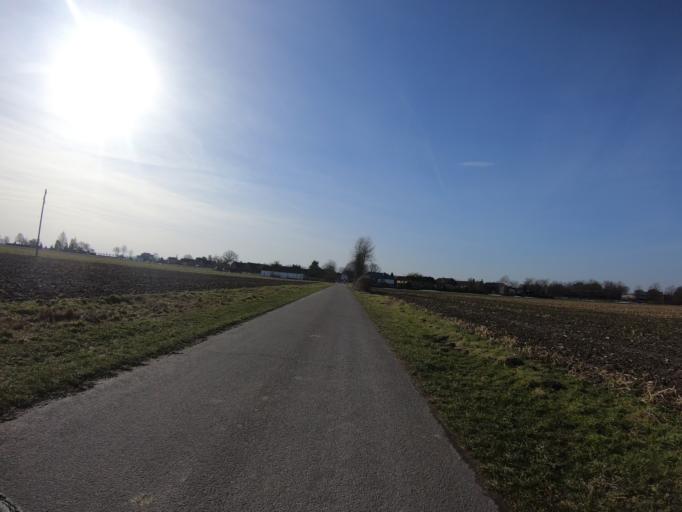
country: DE
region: Lower Saxony
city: Meine
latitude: 52.3862
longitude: 10.5504
